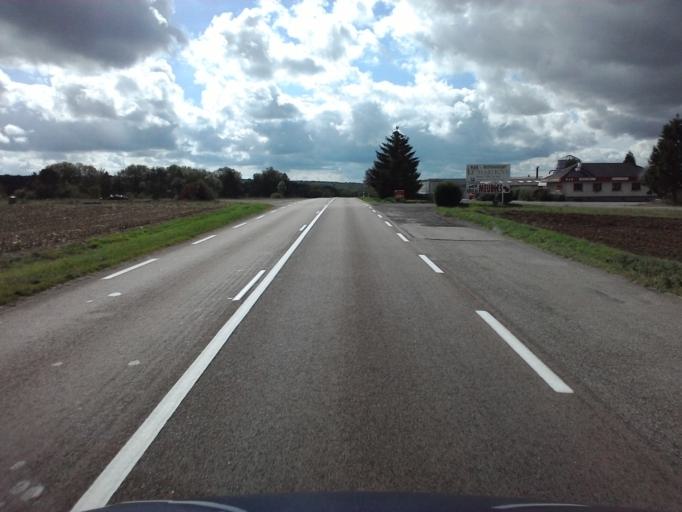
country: FR
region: Lorraine
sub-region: Departement de Meurthe-et-Moselle
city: Colombey-les-Belles
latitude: 48.4509
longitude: 5.8037
